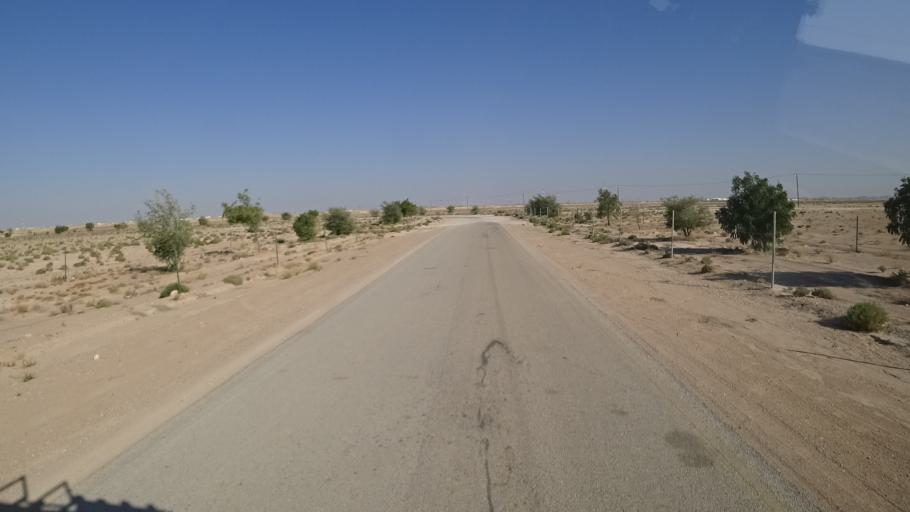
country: OM
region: Zufar
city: Salalah
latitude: 17.5947
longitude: 54.0309
